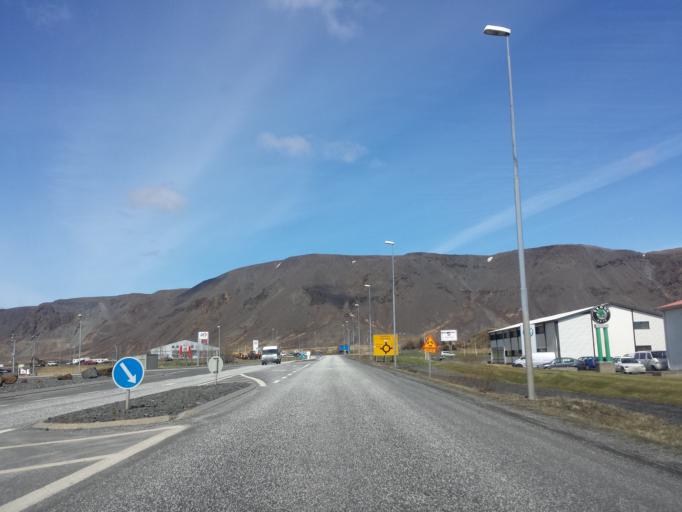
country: IS
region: South
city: Selfoss
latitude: 63.9460
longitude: -21.0112
